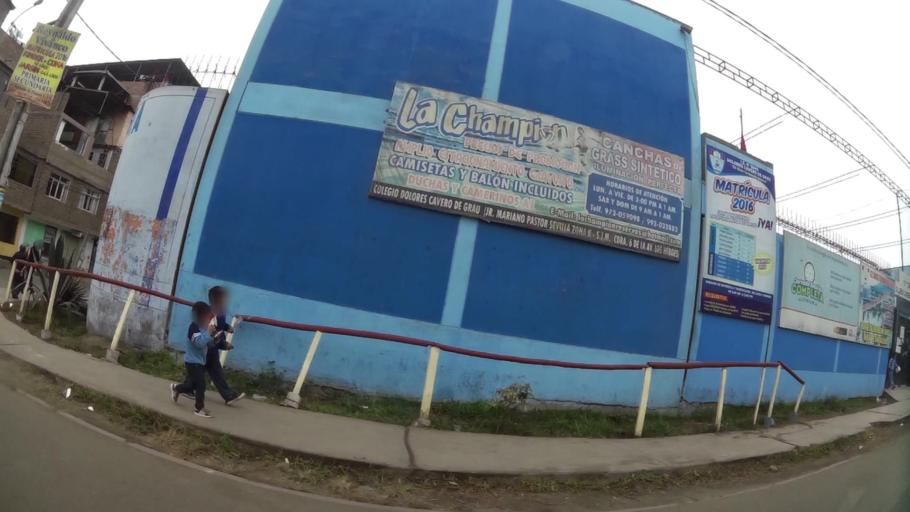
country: PE
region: Lima
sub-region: Lima
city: Surco
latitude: -12.1535
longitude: -76.9673
